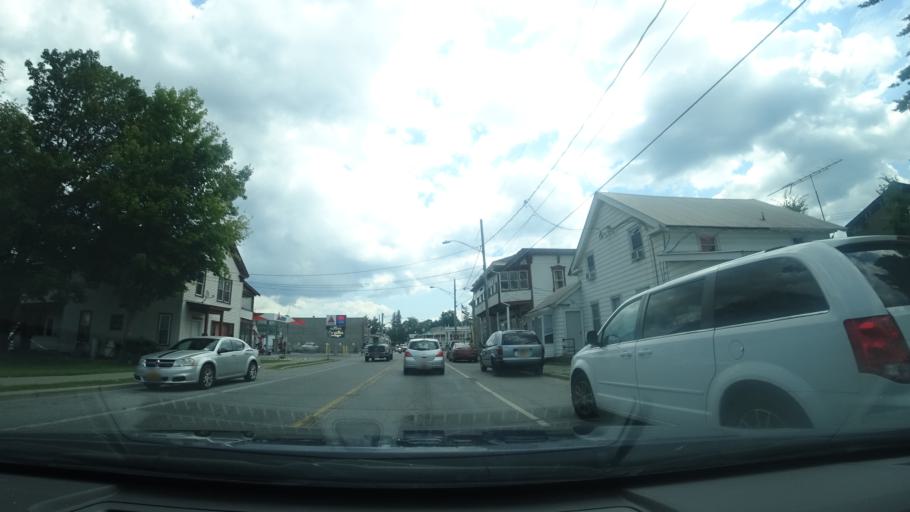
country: US
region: New York
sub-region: Warren County
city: Warrensburg
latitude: 43.4972
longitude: -73.7768
